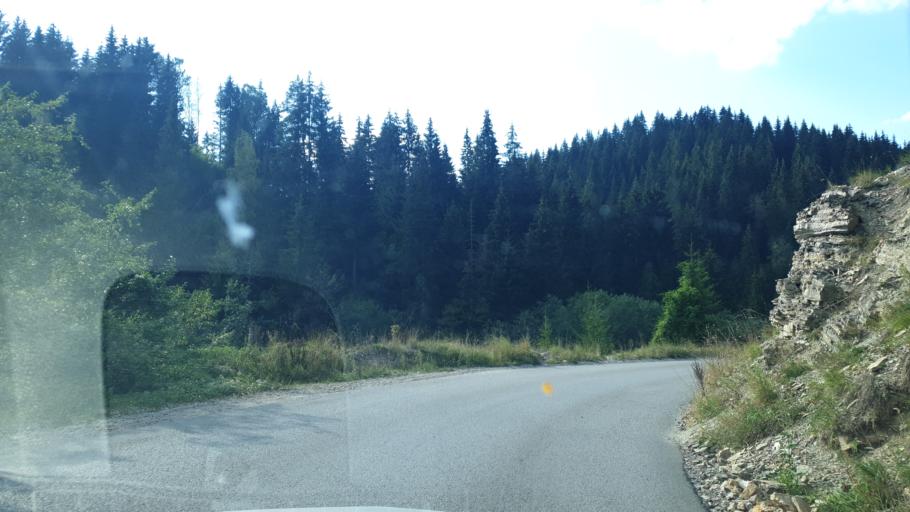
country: RS
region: Central Serbia
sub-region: Zlatiborski Okrug
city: Nova Varos
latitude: 43.4396
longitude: 19.8537
